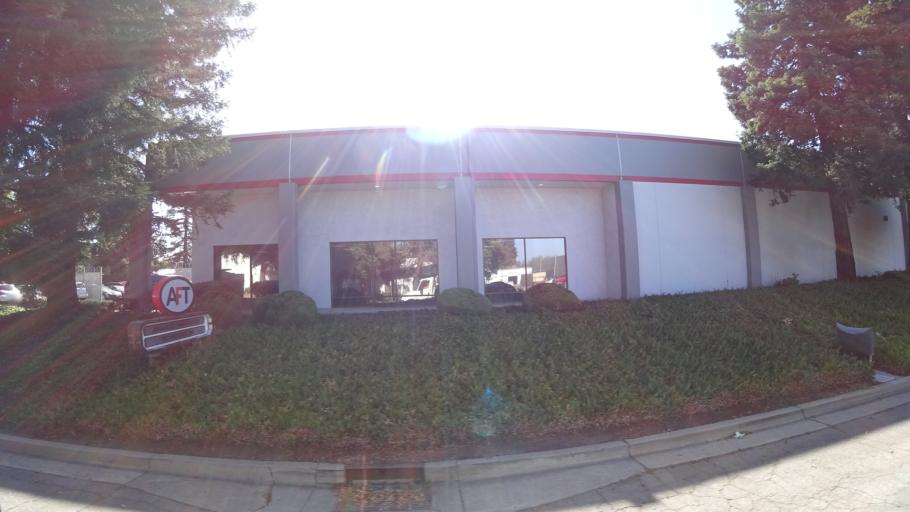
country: US
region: California
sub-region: Alameda County
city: Union City
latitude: 37.6095
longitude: -122.0510
